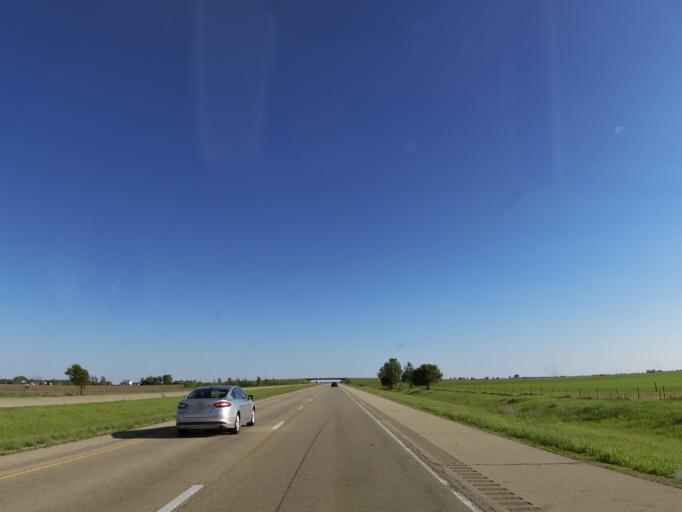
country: US
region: Illinois
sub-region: Woodford County
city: Minonk
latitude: 40.8311
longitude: -89.0363
